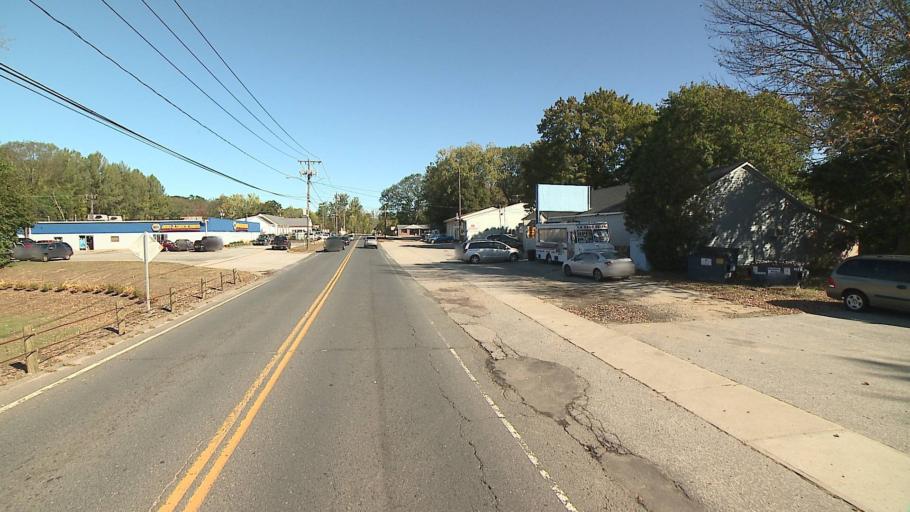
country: US
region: Connecticut
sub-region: Windham County
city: Willimantic
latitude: 41.7181
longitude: -72.1965
